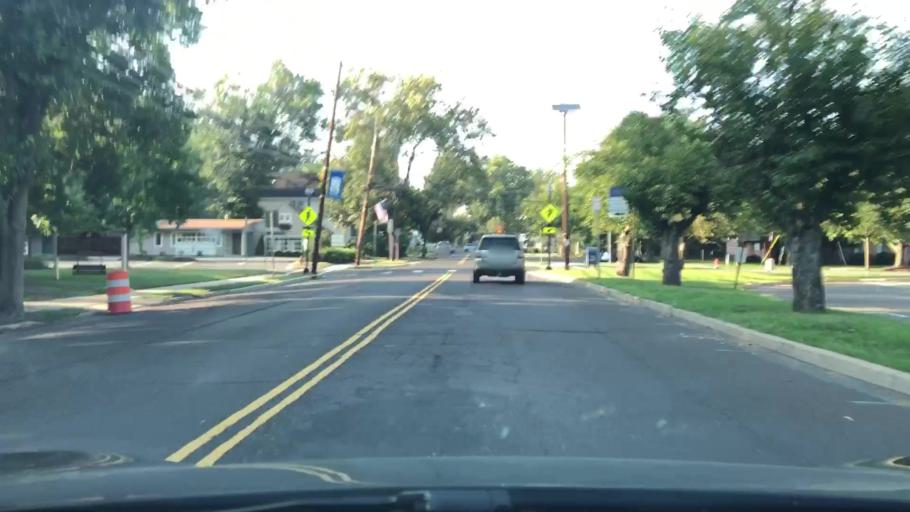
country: US
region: New Jersey
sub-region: Mercer County
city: Pennington
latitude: 40.3209
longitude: -74.7903
